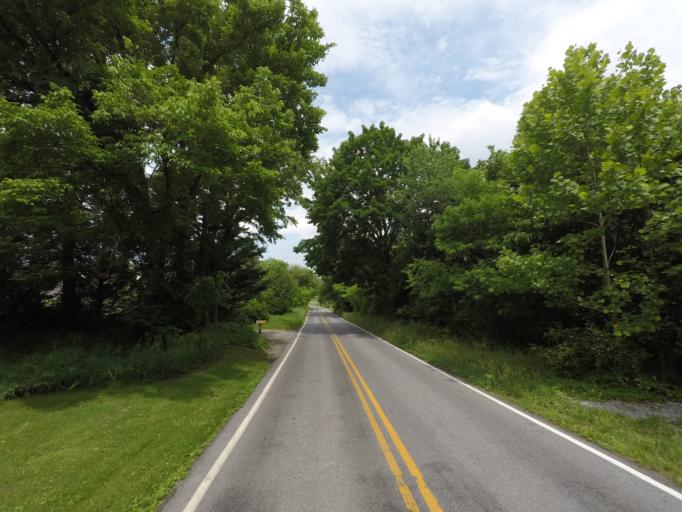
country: US
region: Maryland
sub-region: Washington County
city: Keedysville
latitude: 39.4610
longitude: -77.7091
